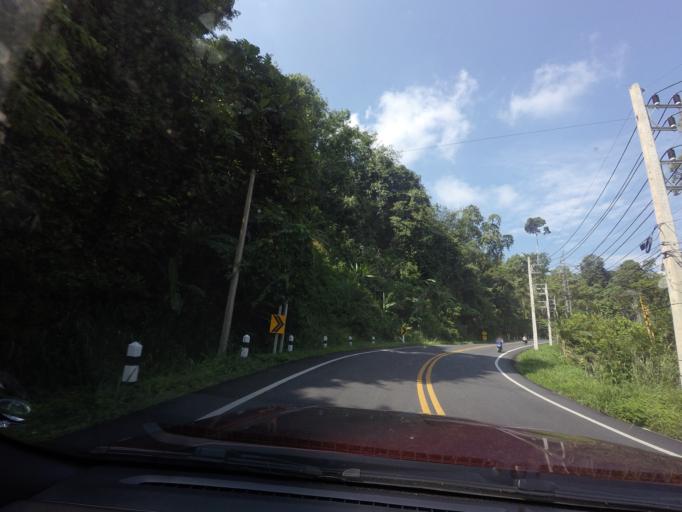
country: TH
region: Yala
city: Betong
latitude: 5.9128
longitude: 101.1560
